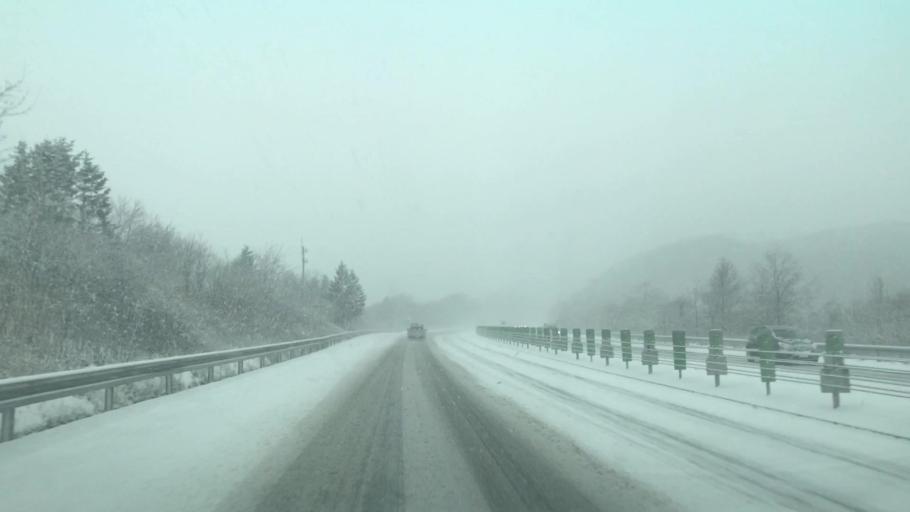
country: JP
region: Hokkaido
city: Shiraoi
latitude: 42.5005
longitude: 141.2639
